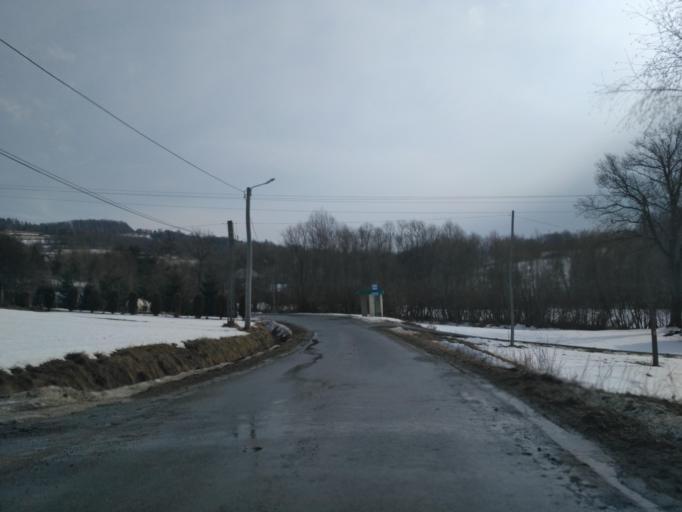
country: PL
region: Subcarpathian Voivodeship
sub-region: Powiat brzozowski
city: Dydnia
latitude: 49.6514
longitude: 22.1526
